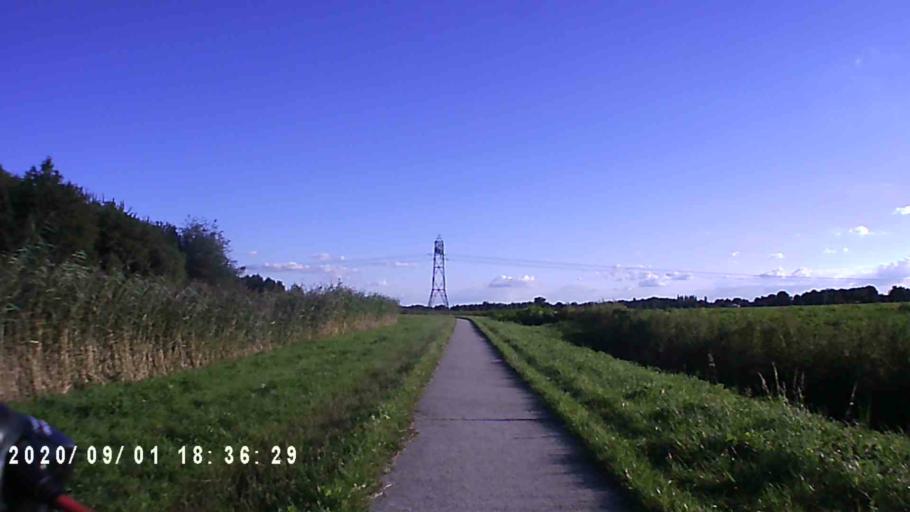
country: NL
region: Groningen
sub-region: Gemeente Hoogezand-Sappemeer
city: Sappemeer
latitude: 53.1489
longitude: 6.8068
